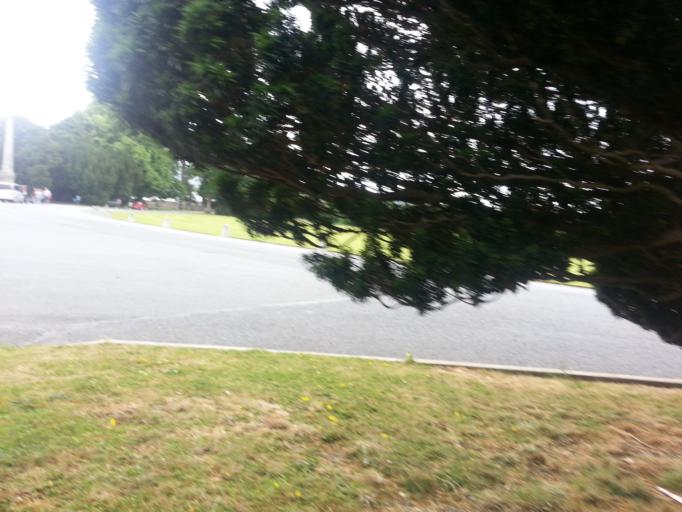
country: IE
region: Leinster
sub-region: Wicklow
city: Enniskerry
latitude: 53.1855
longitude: -6.1866
